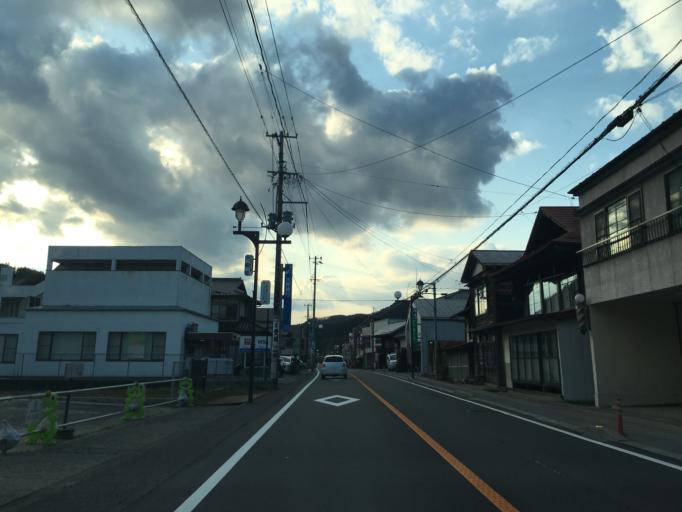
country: JP
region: Fukushima
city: Ishikawa
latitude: 37.0927
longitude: 140.5499
